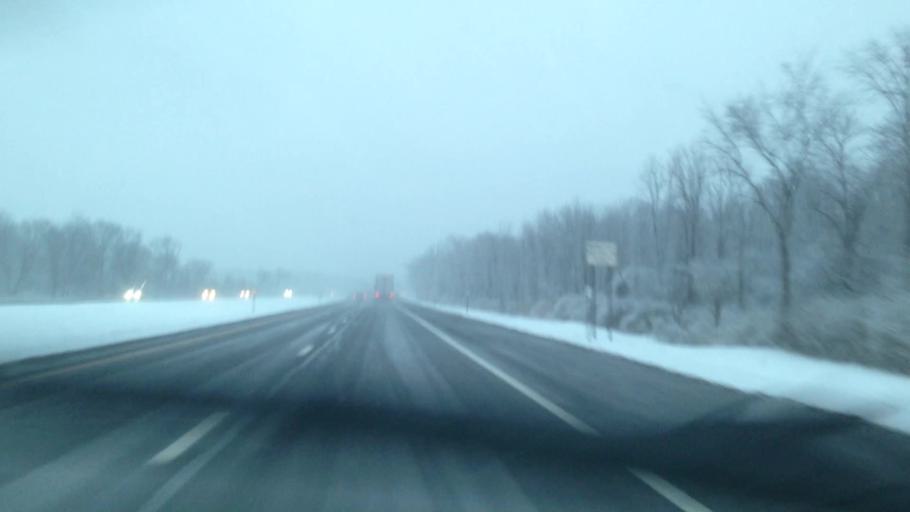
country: US
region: New York
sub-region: Madison County
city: Canastota
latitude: 43.0975
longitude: -75.7360
